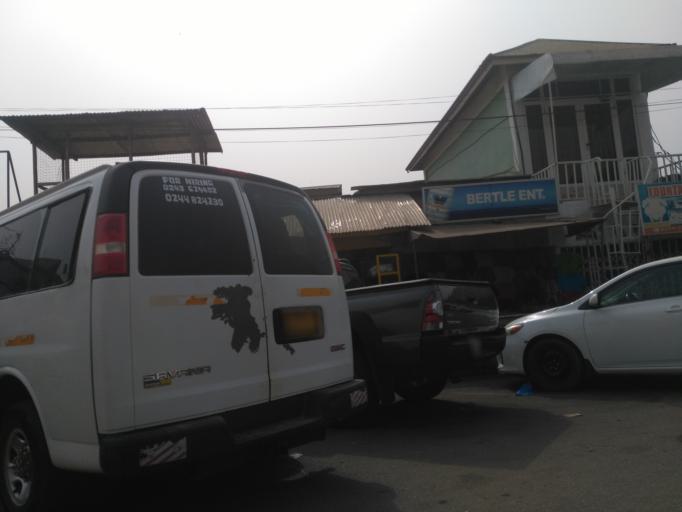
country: GH
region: Ashanti
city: Kumasi
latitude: 6.6870
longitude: -1.6156
